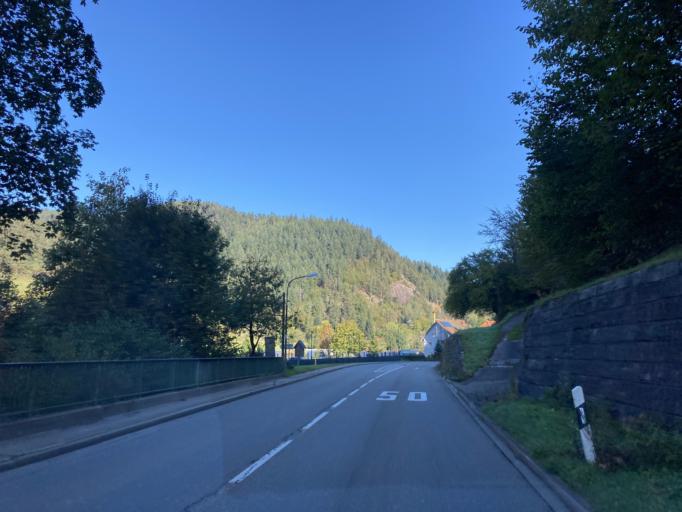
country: DE
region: Baden-Wuerttemberg
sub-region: Freiburg Region
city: Hornberg
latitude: 48.1906
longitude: 8.2307
